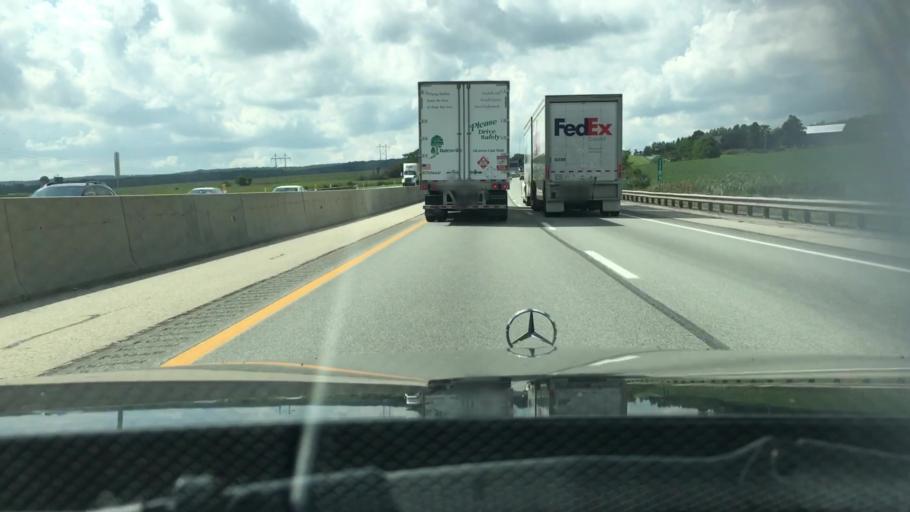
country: US
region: Pennsylvania
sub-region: Somerset County
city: Berlin
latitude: 39.9771
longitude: -78.9336
